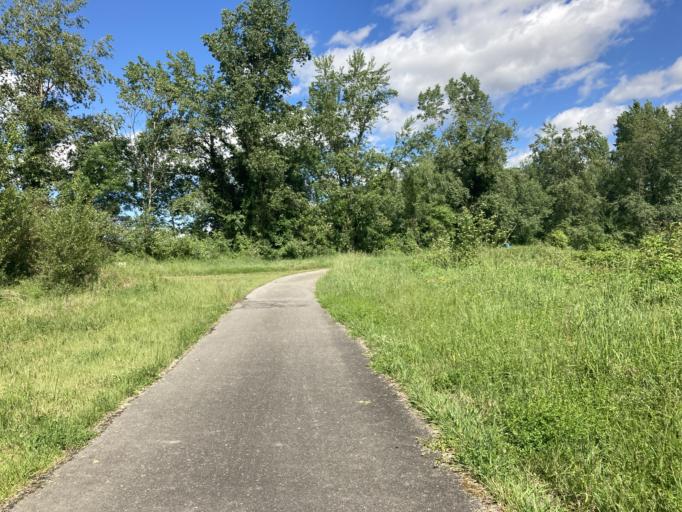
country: FR
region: Aquitaine
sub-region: Departement des Pyrenees-Atlantiques
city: Arbus
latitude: 43.3334
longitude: -0.4882
